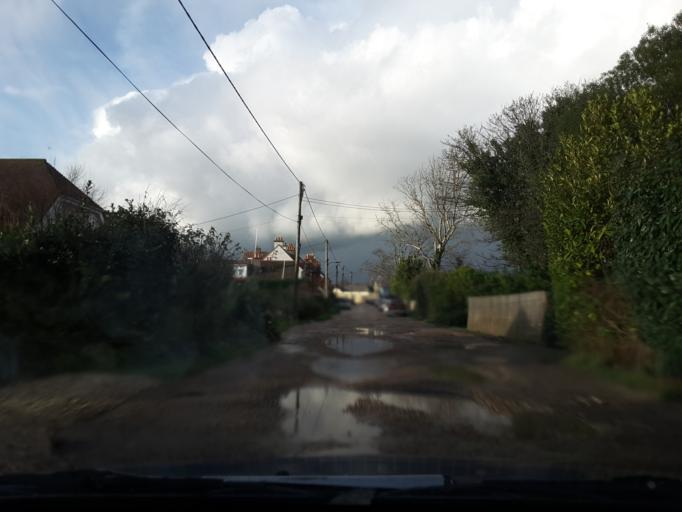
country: GB
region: England
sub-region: Isle of Wight
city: Bembridge
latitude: 50.6869
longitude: -1.0867
